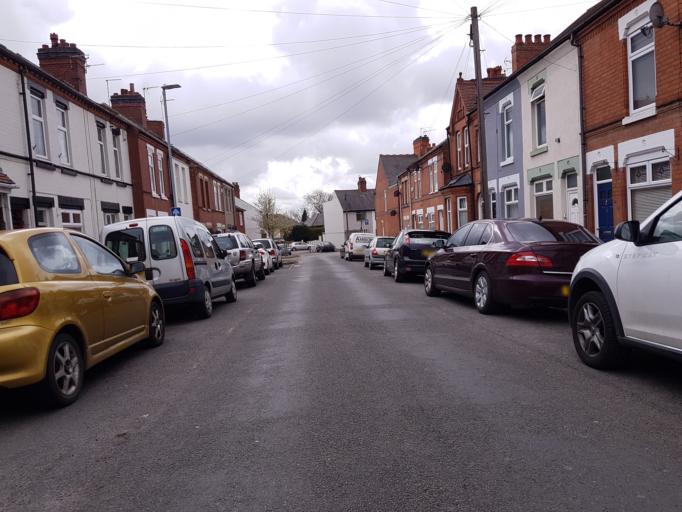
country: GB
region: England
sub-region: Leicestershire
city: Hinckley
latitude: 52.5402
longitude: -1.3661
